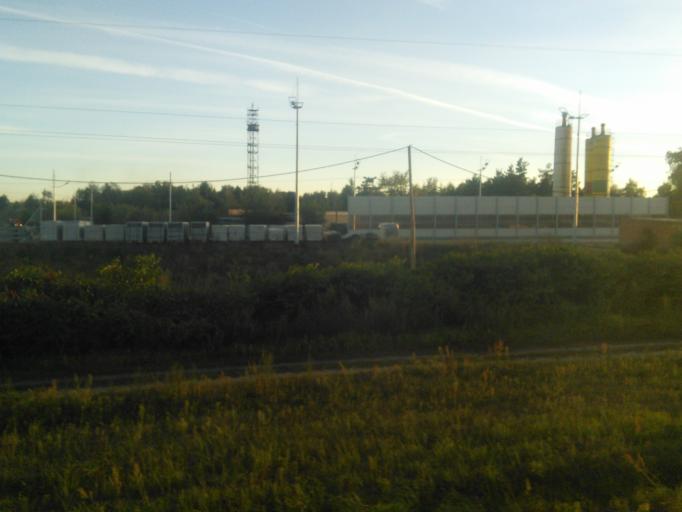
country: RU
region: Moskovskaya
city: Kupavna
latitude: 55.7427
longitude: 38.1582
